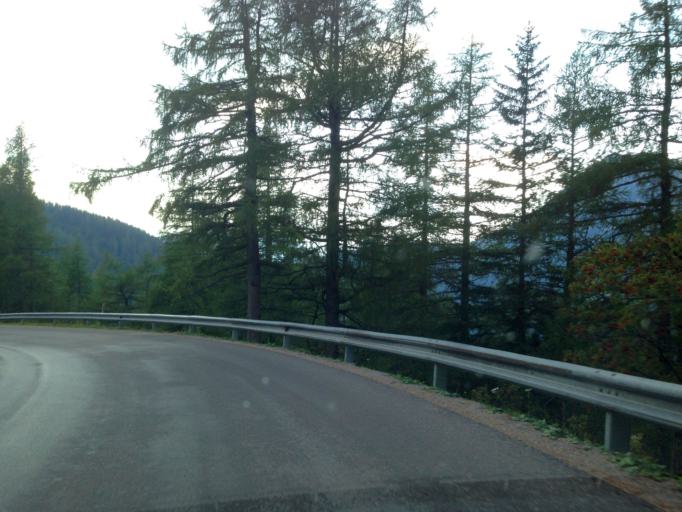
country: AT
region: Styria
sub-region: Politischer Bezirk Liezen
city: Schladming
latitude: 47.4498
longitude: 13.6108
